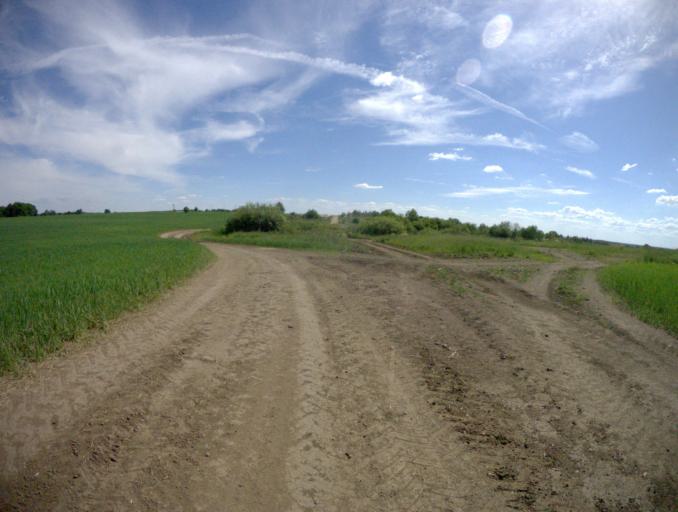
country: RU
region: Vladimir
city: Stavrovo
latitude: 56.2801
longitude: 40.0494
